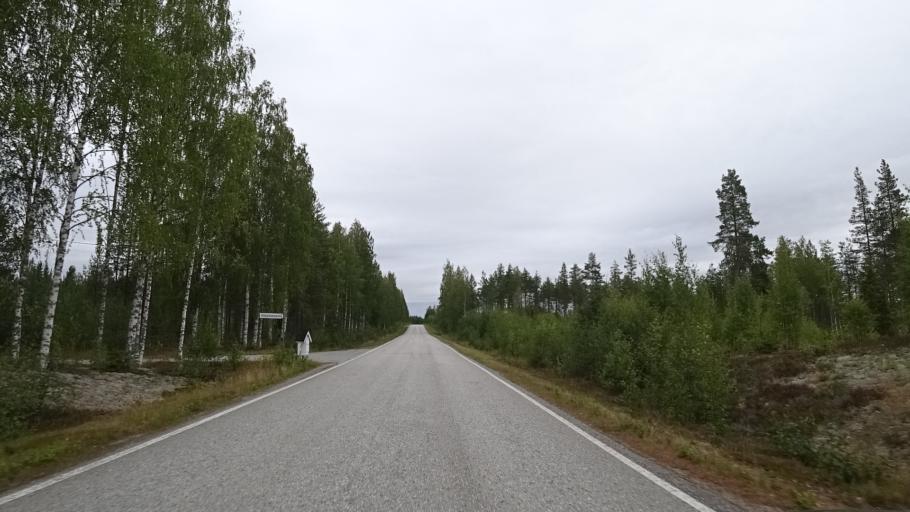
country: FI
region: North Karelia
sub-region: Pielisen Karjala
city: Lieksa
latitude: 63.3516
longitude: 30.2652
